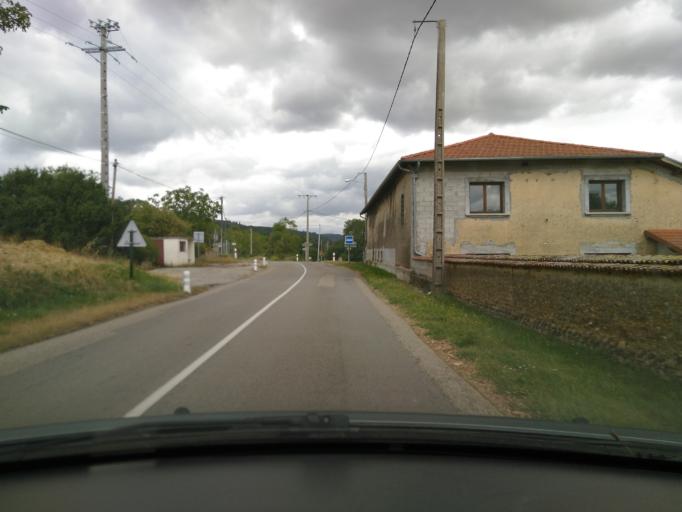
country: FR
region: Rhone-Alpes
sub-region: Departement de l'Isere
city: Saint-Jean-de-Bournay
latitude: 45.4151
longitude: 5.1523
